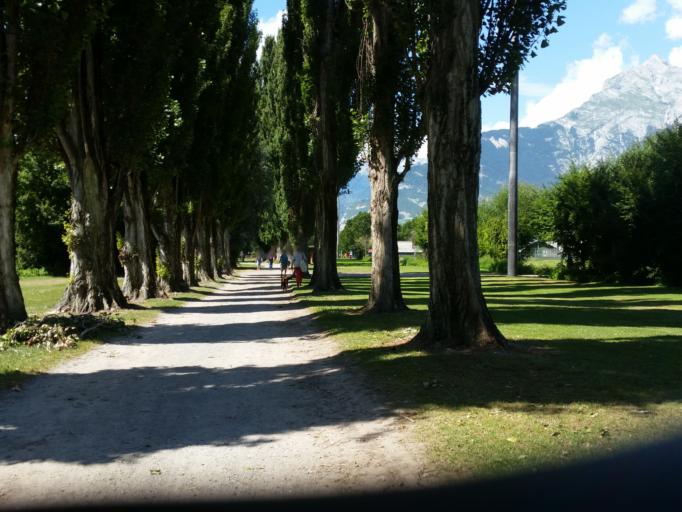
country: CH
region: Valais
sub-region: Conthey District
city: Conthey
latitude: 46.2135
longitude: 7.3255
